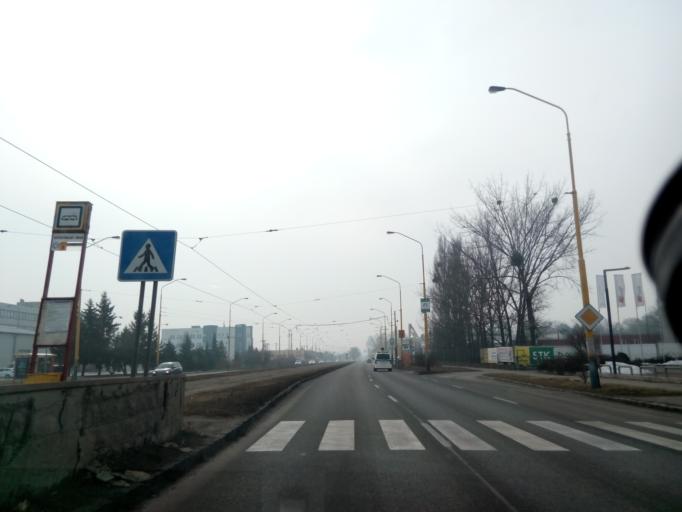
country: SK
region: Kosicky
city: Kosice
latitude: 48.6826
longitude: 21.2677
